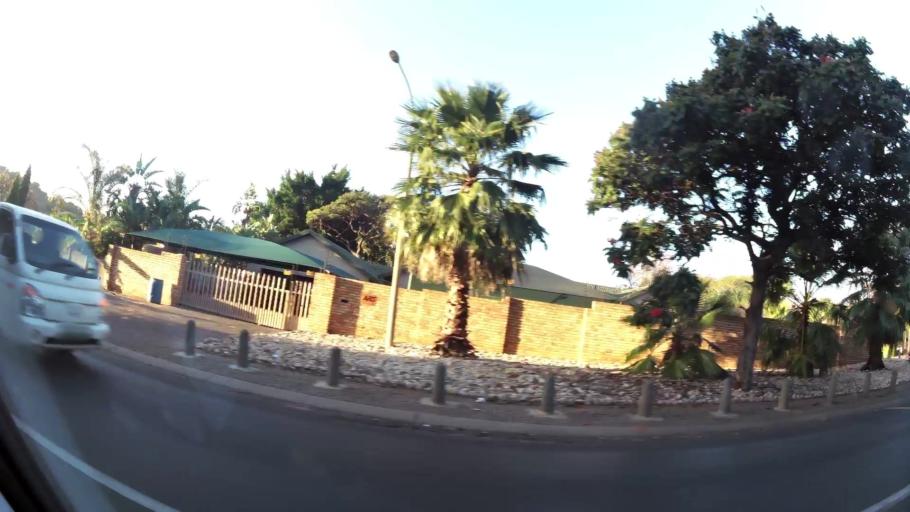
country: ZA
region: North-West
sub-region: Bojanala Platinum District Municipality
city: Rustenburg
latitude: -25.7012
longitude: 27.2338
